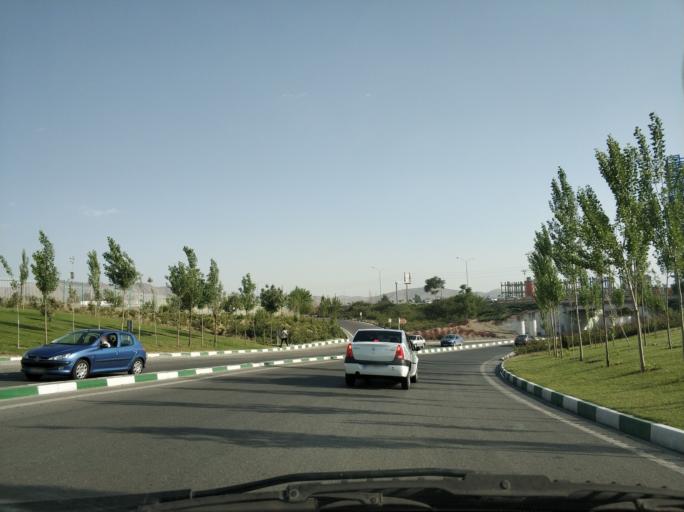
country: IR
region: Tehran
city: Tajrish
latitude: 35.7543
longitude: 51.5783
